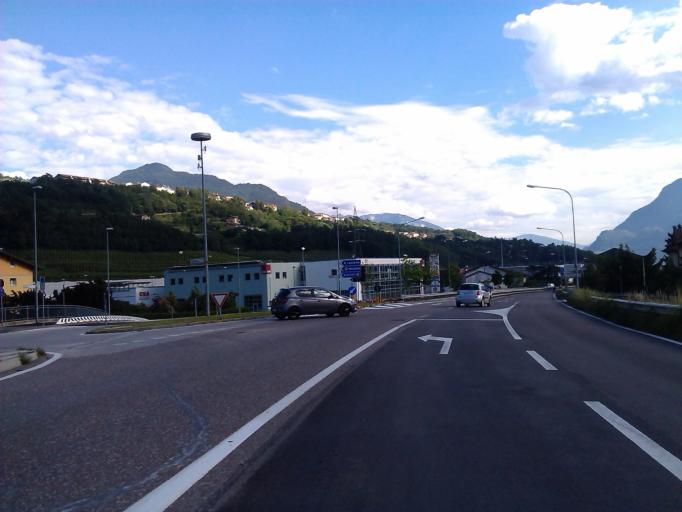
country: IT
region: Trentino-Alto Adige
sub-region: Provincia di Trento
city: Lavis
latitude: 46.1344
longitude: 11.1110
